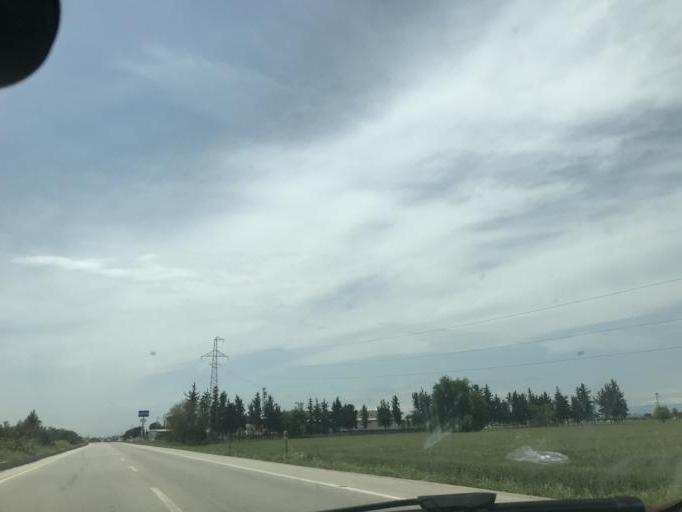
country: TR
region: Adana
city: Yakapinar
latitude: 36.9750
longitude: 35.4925
